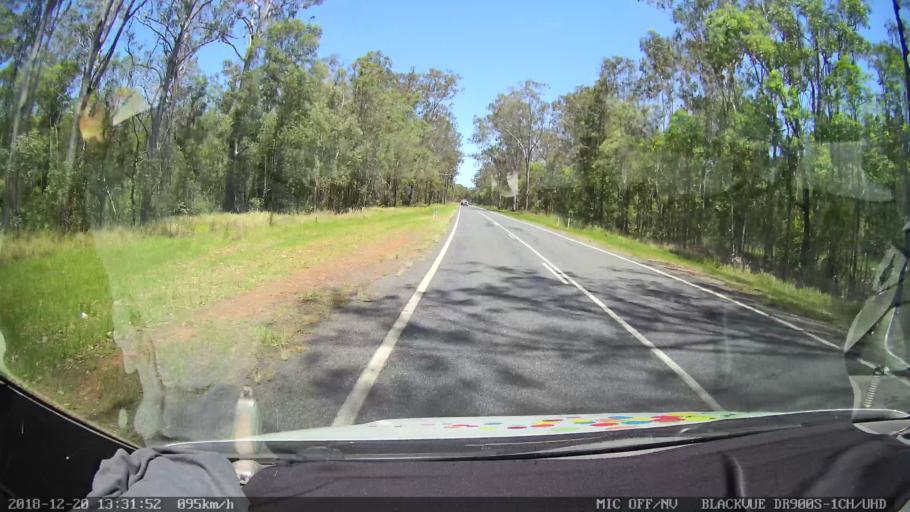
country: AU
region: New South Wales
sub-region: Clarence Valley
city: Gordon
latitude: -29.2242
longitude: 152.9876
